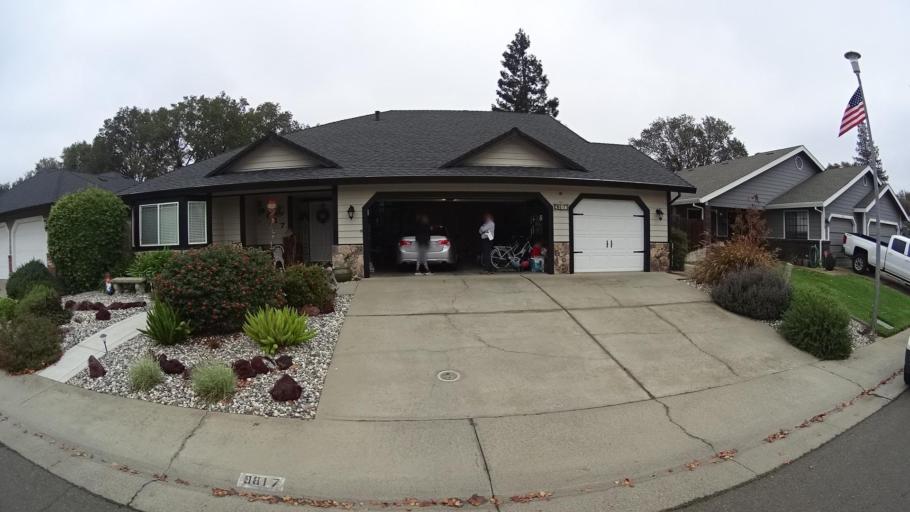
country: US
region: California
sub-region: Sacramento County
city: Elk Grove
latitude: 38.4011
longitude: -121.3627
